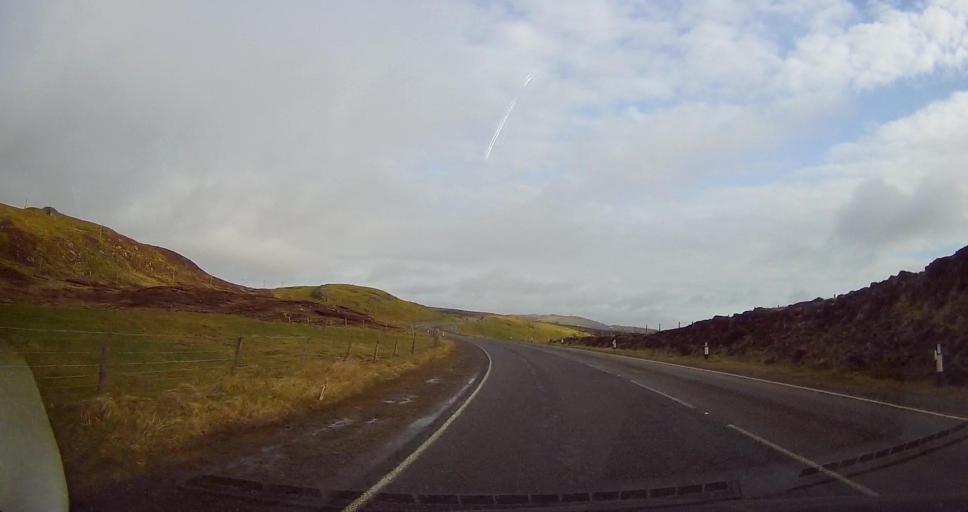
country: GB
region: Scotland
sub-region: Shetland Islands
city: Lerwick
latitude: 60.1060
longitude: -1.2192
